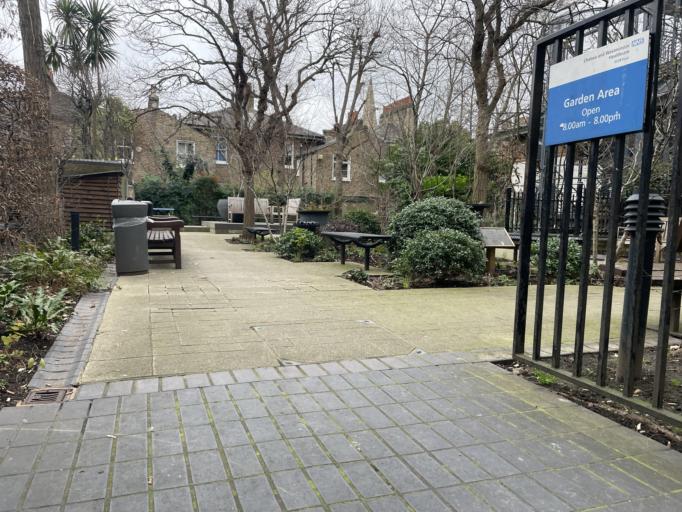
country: GB
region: England
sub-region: Greater London
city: Chelsea
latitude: 51.4846
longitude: -0.1807
